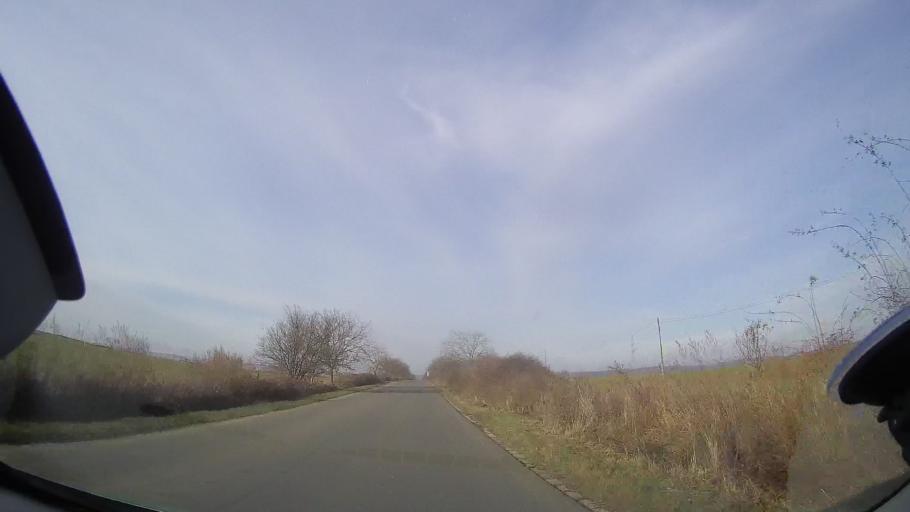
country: RO
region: Bihor
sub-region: Comuna Spinus
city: Spinus
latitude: 47.2186
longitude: 22.1733
